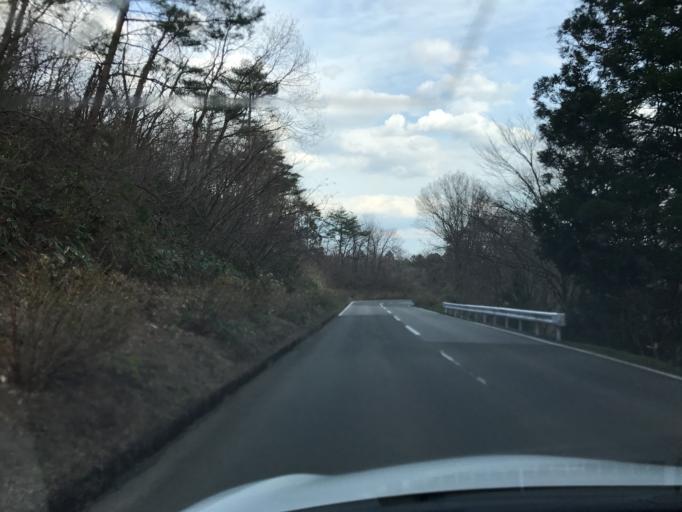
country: JP
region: Miyagi
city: Shiroishi
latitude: 38.0211
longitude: 140.5681
